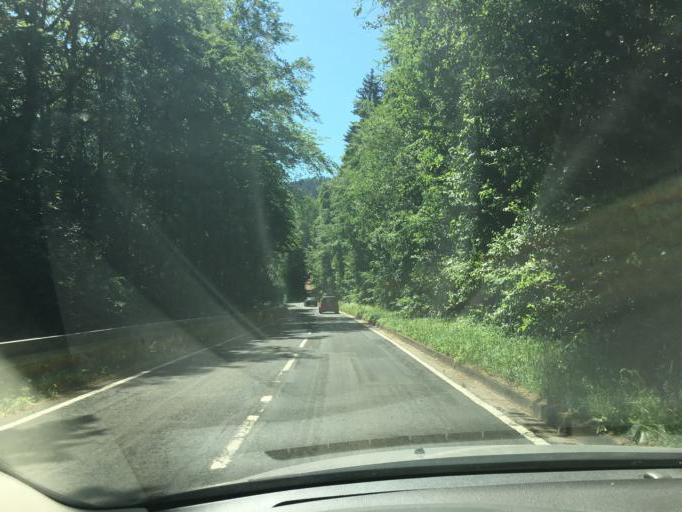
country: DE
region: Hesse
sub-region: Regierungsbezirk Kassel
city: Malsfeld
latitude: 51.0764
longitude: 9.5456
